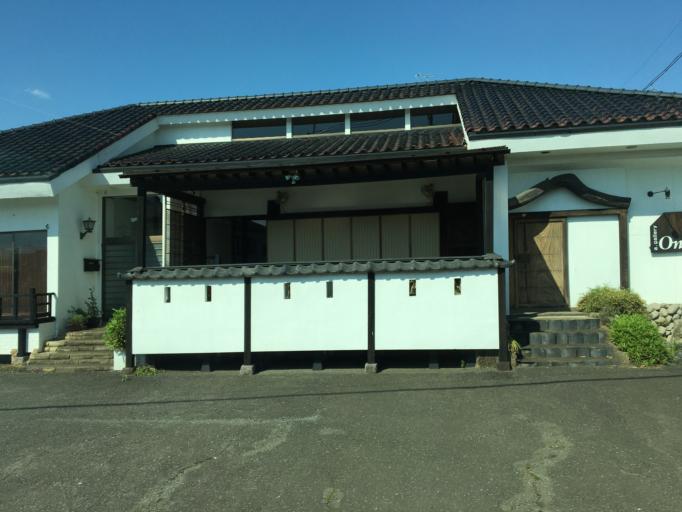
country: JP
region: Saitama
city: Morohongo
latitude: 35.9751
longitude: 139.3380
